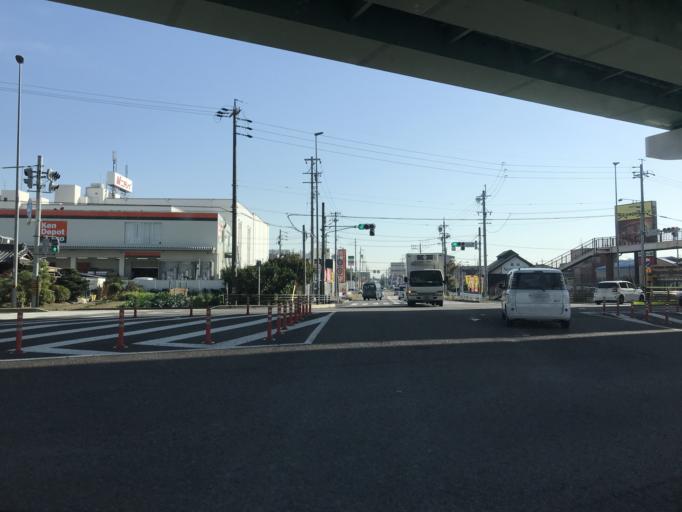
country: JP
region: Aichi
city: Iwakura
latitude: 35.2299
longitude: 136.8514
